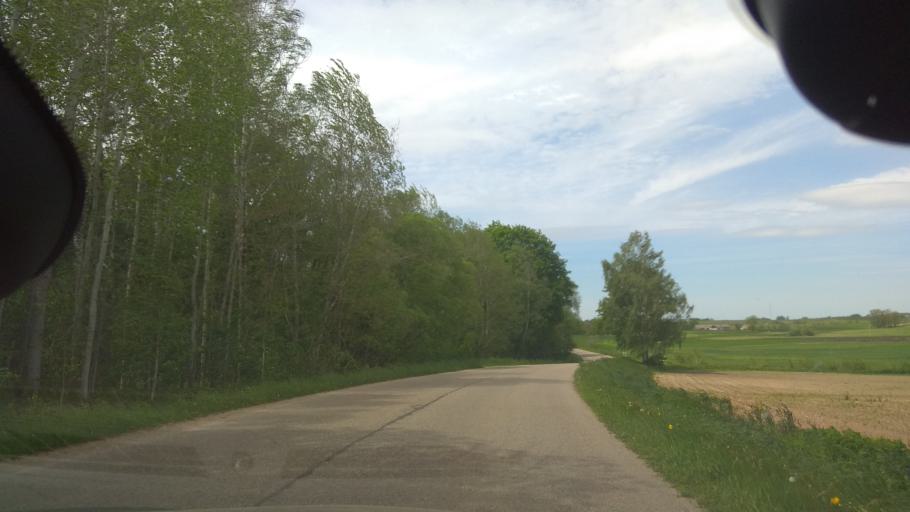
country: LT
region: Vilnius County
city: Ukmerge
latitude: 55.1509
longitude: 24.5508
